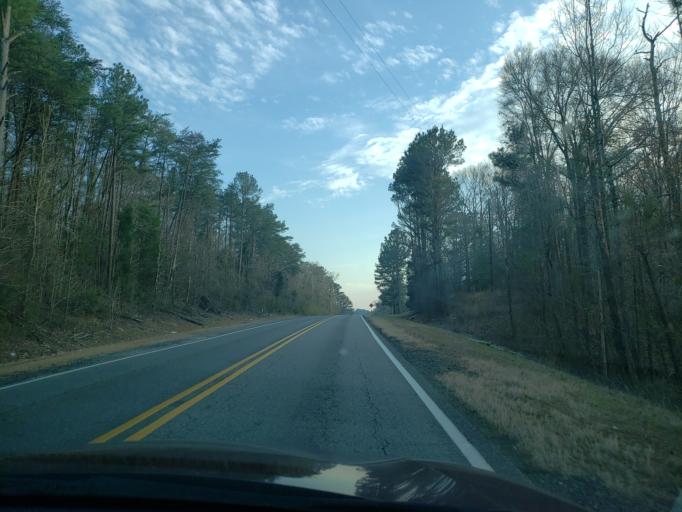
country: US
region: Alabama
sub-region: Hale County
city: Greensboro
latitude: 32.7463
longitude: -87.5851
